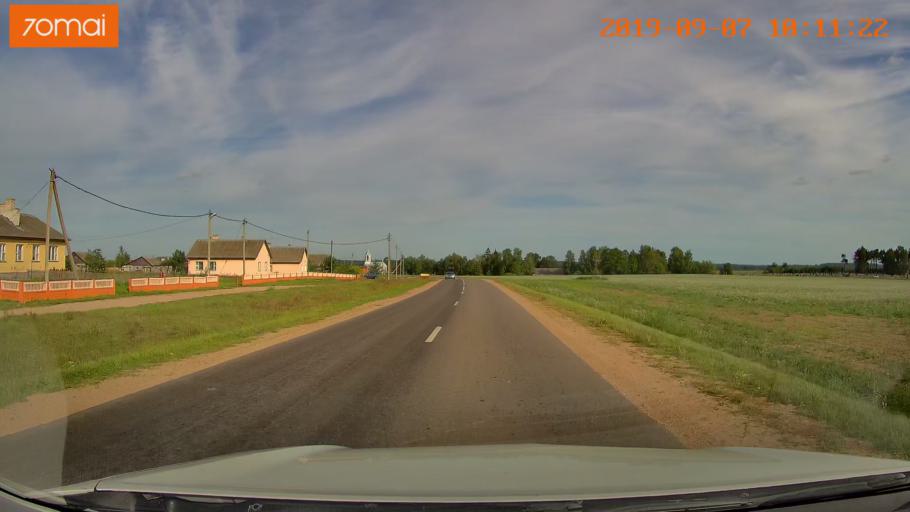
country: BY
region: Grodnenskaya
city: Voranava
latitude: 54.1221
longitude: 25.3666
